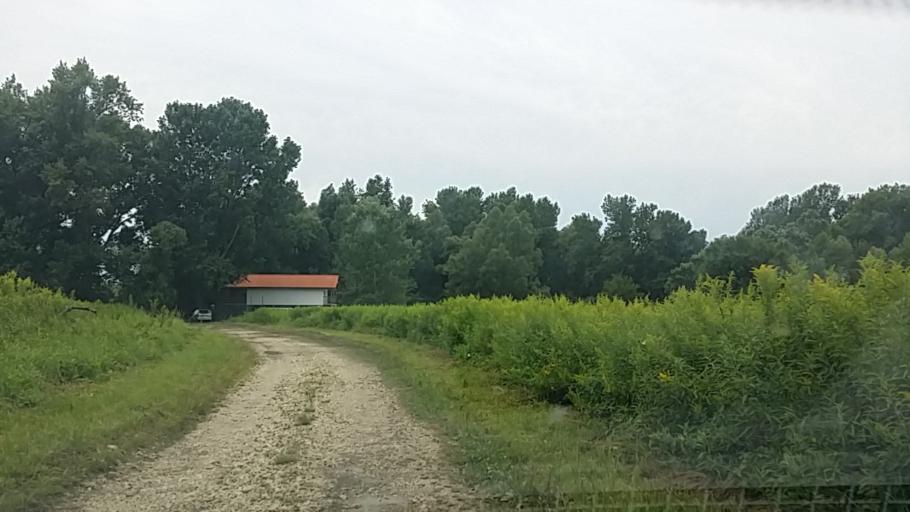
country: HR
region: Medimurska
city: Domasinec
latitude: 46.4666
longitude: 16.6409
